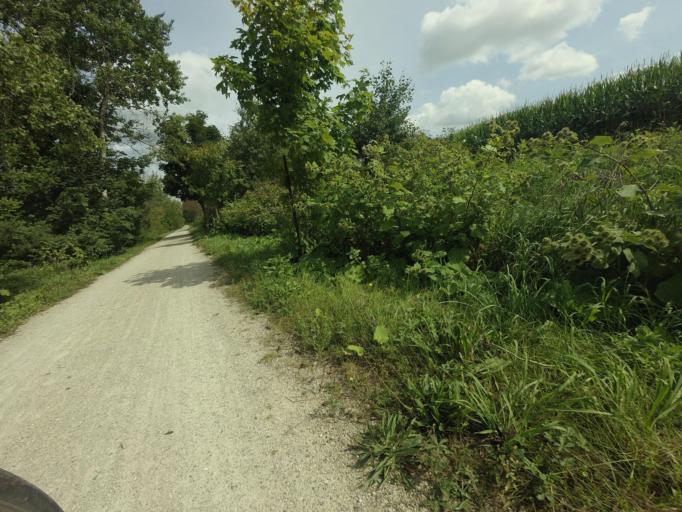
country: CA
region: Ontario
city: Waterloo
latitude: 43.6138
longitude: -80.5816
